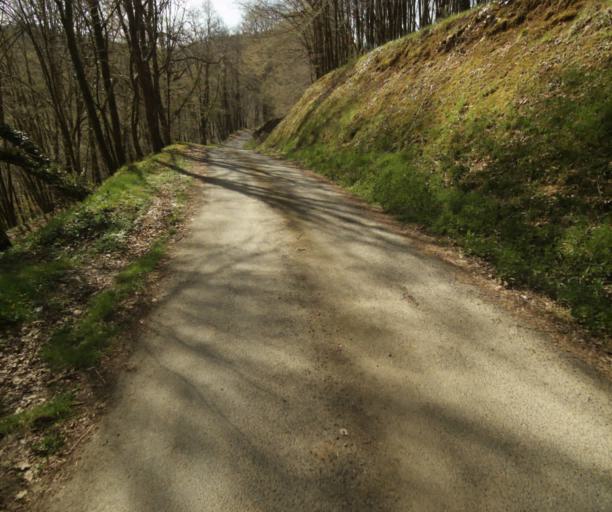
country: FR
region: Limousin
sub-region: Departement de la Correze
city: Naves
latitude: 45.3414
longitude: 1.7854
